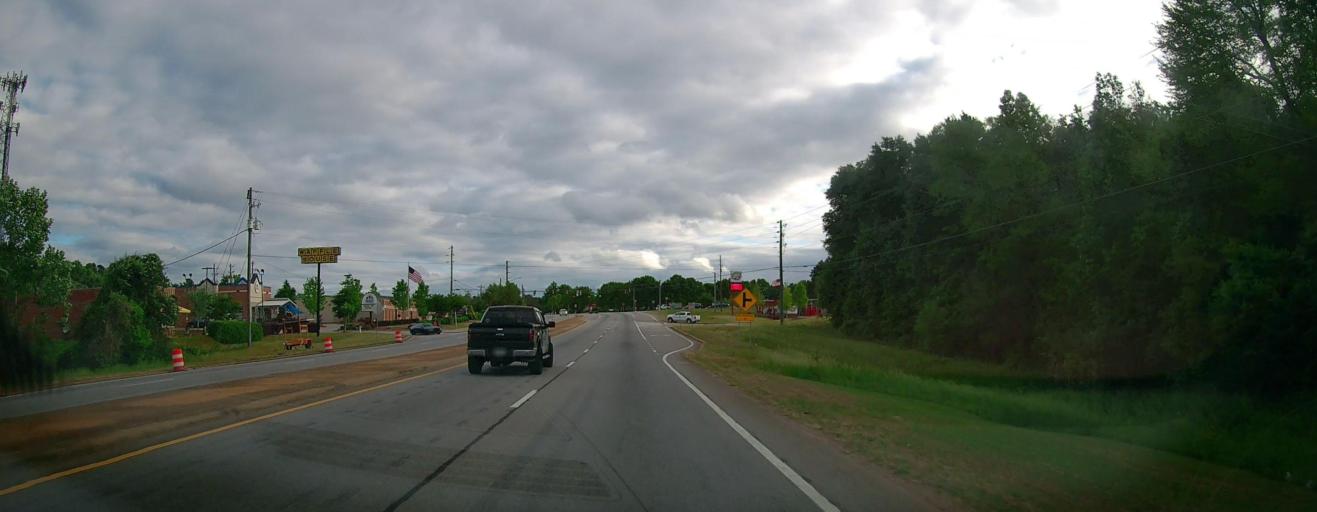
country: US
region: Georgia
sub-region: Oconee County
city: Watkinsville
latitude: 33.8909
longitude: -83.4128
